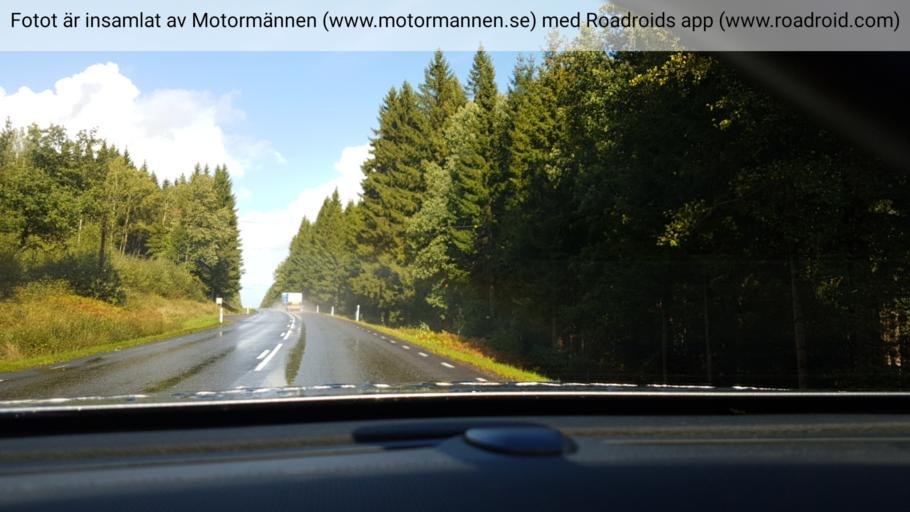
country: SE
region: Vaestra Goetaland
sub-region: Alingsas Kommun
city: Sollebrunn
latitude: 58.0246
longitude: 12.4598
